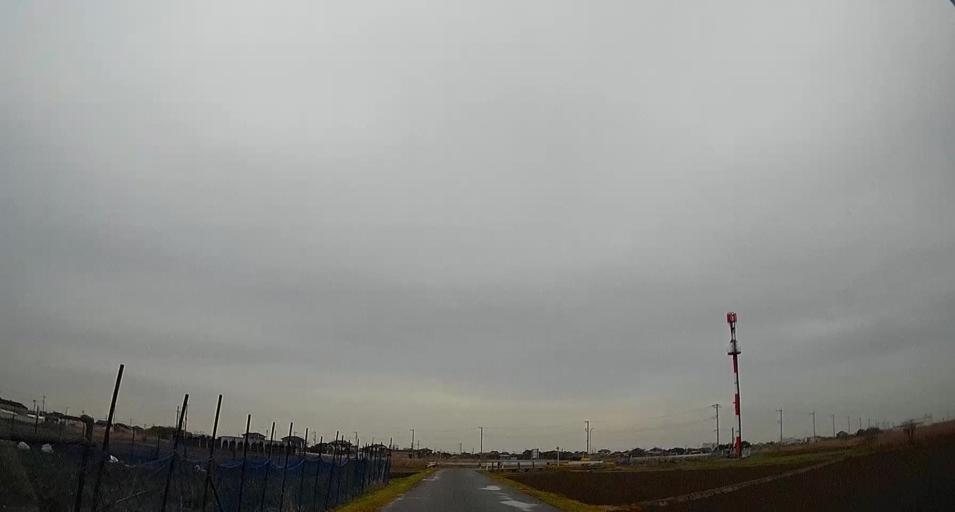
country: JP
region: Chiba
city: Kisarazu
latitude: 35.4239
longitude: 139.9095
